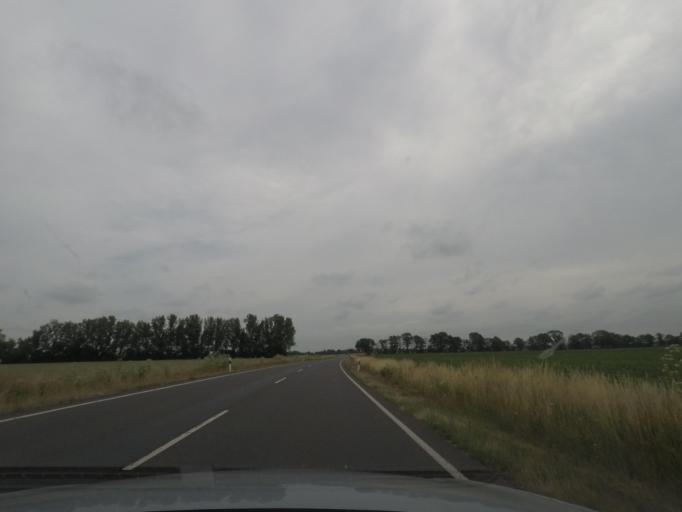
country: DE
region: Saxony-Anhalt
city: Hohendodeleben
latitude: 52.0769
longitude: 11.5019
